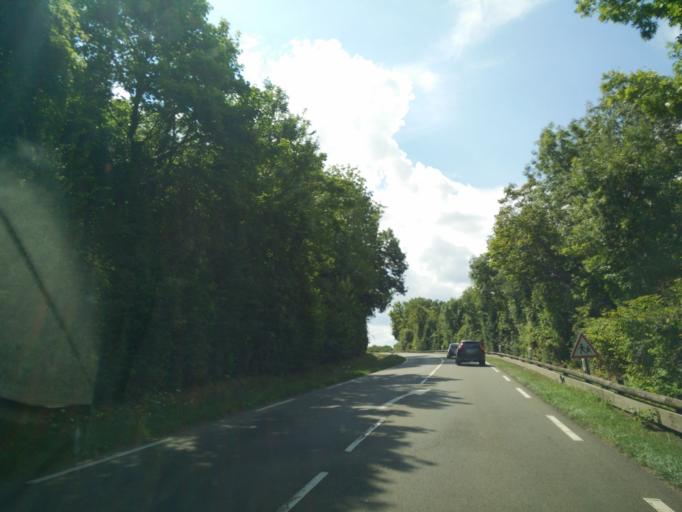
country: FR
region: Ile-de-France
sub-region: Departement des Yvelines
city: Mantes-la-Ville
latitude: 48.9582
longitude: 1.7161
